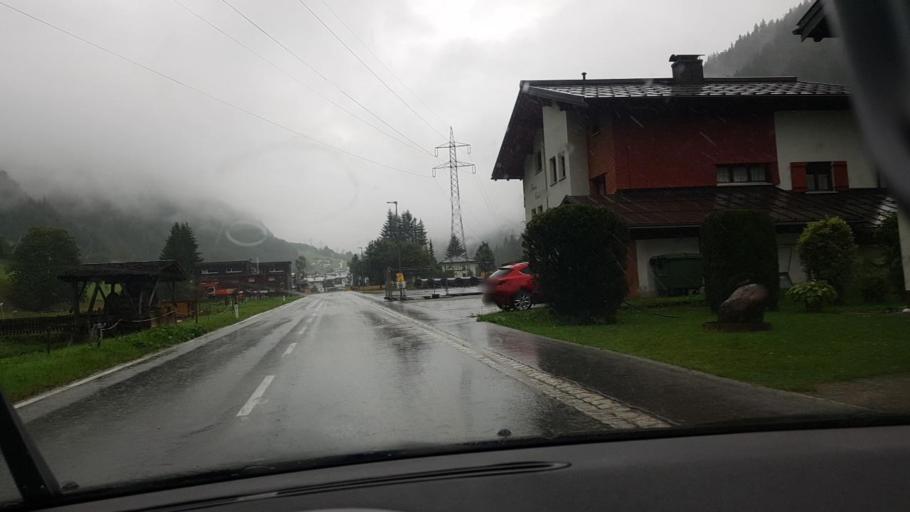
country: AT
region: Vorarlberg
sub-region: Politischer Bezirk Bludenz
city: Klosterle
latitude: 47.1315
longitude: 10.0809
